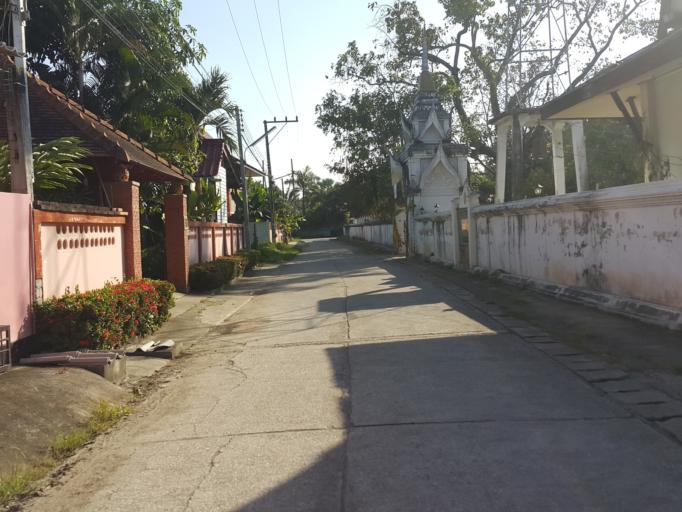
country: TH
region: Chiang Mai
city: San Kamphaeng
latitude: 18.8035
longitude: 99.1149
